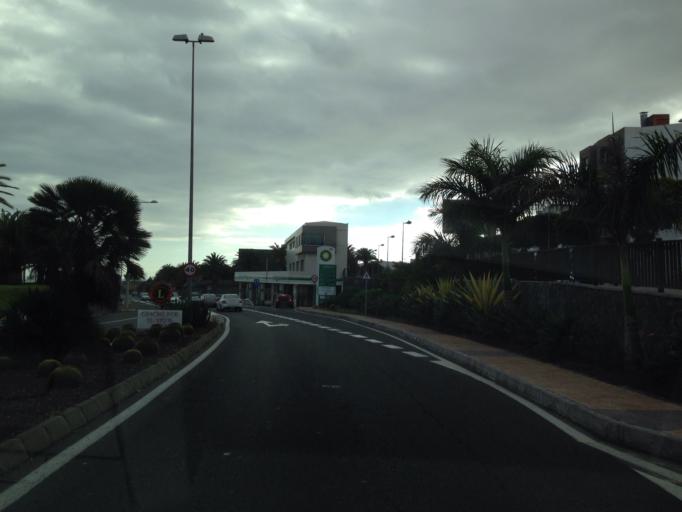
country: ES
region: Canary Islands
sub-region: Provincia de Las Palmas
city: Cruce de Arinaga
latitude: 27.8361
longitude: -15.4505
